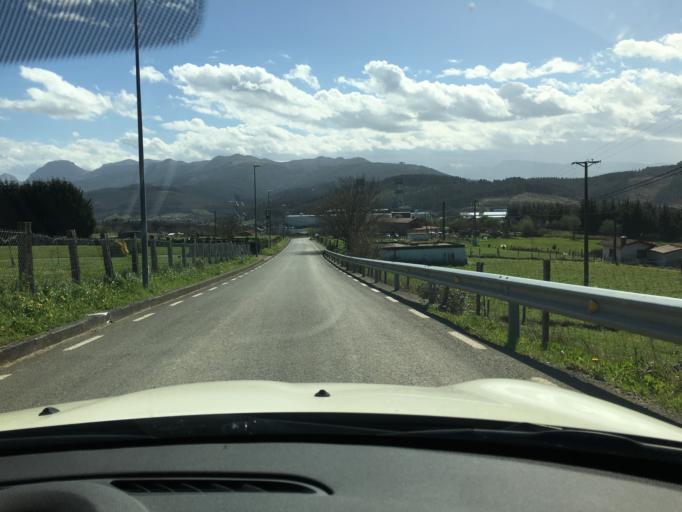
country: ES
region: Basque Country
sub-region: Bizkaia
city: Amorebieta
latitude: 43.2399
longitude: -2.7502
